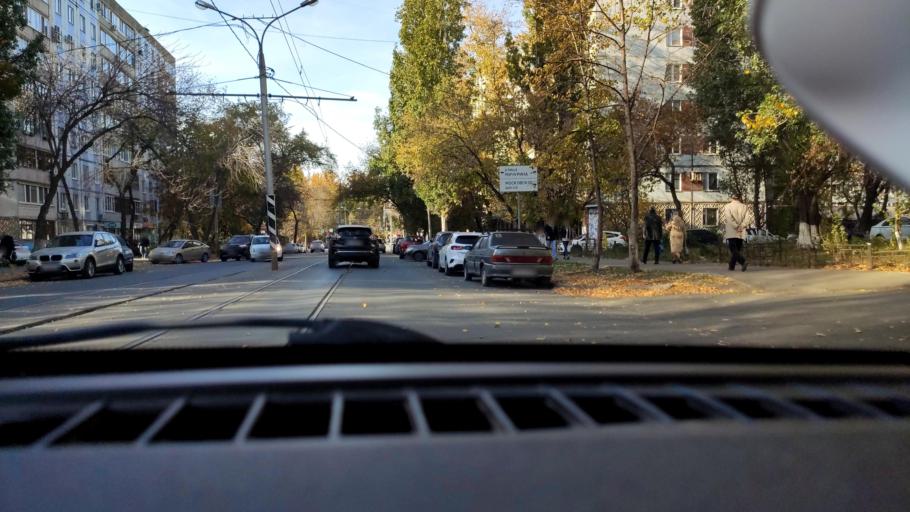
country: RU
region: Samara
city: Samara
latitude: 53.2002
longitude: 50.1370
